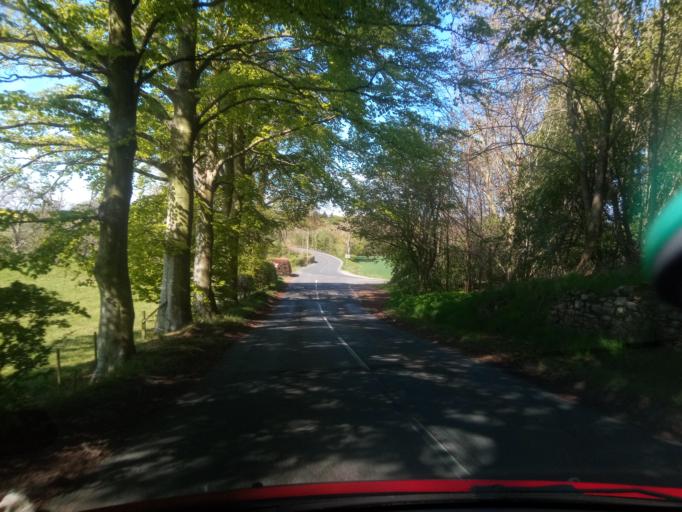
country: GB
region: Scotland
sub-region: The Scottish Borders
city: Jedburgh
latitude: 55.4688
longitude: -2.6450
